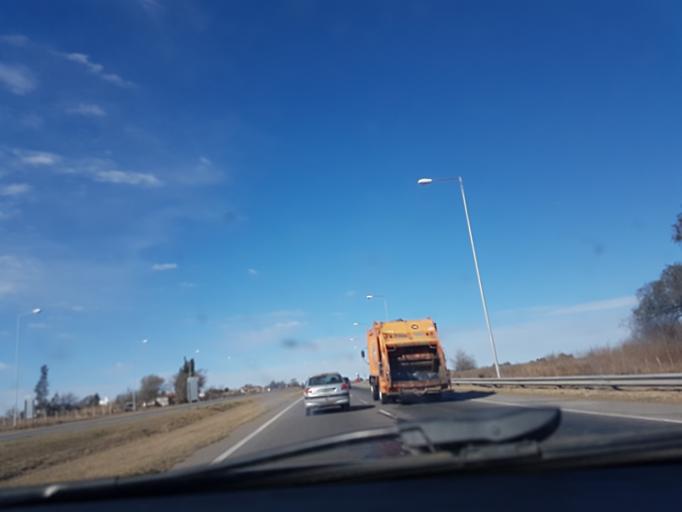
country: AR
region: Cordoba
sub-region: Departamento de Capital
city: Cordoba
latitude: -31.4151
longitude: -64.2697
